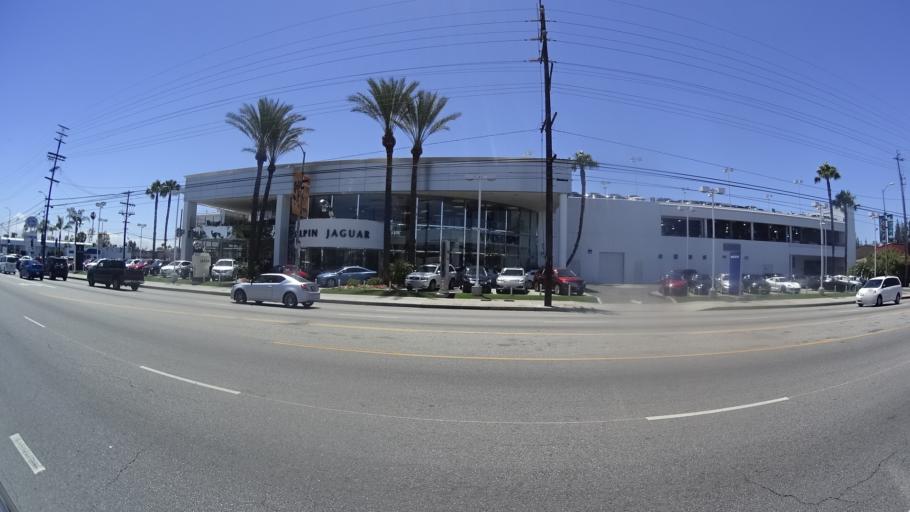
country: US
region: California
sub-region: Los Angeles County
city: Van Nuys
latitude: 34.2215
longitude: -118.4707
